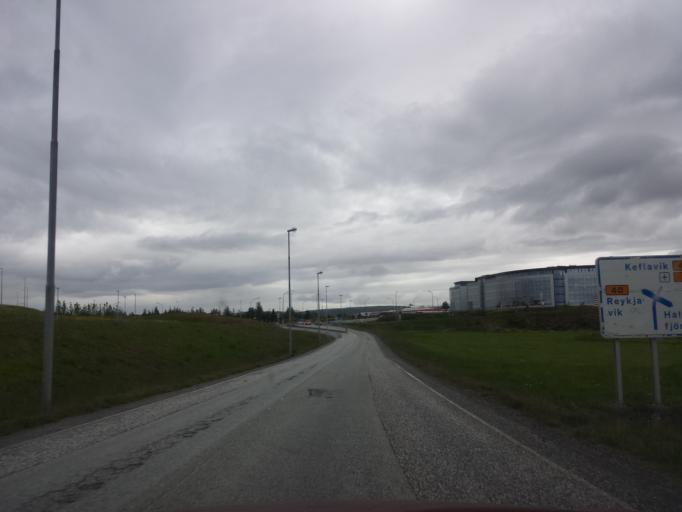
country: IS
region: Capital Region
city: Hafnarfjoerdur
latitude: 64.0846
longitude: -21.9500
